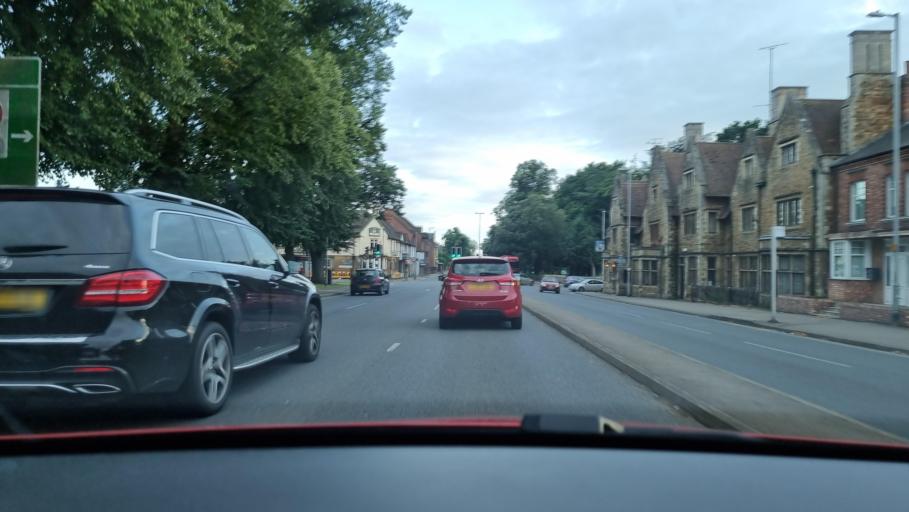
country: GB
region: England
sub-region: Northamptonshire
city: Northampton
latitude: 52.2603
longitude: -0.9004
